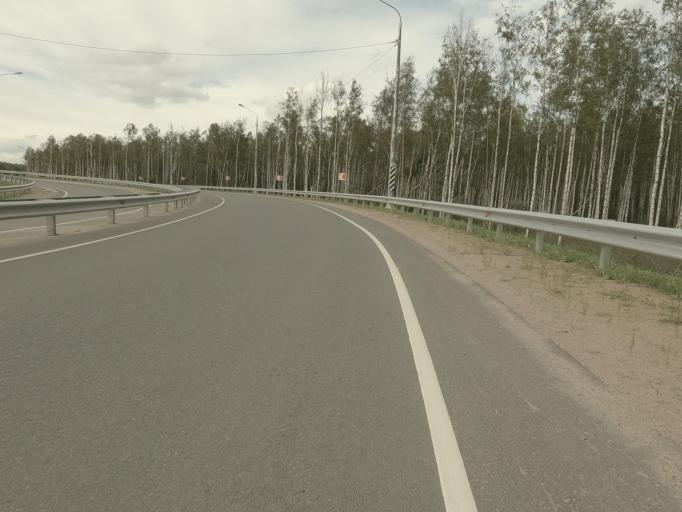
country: RU
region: Leningrad
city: Mga
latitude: 59.7574
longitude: 31.0960
